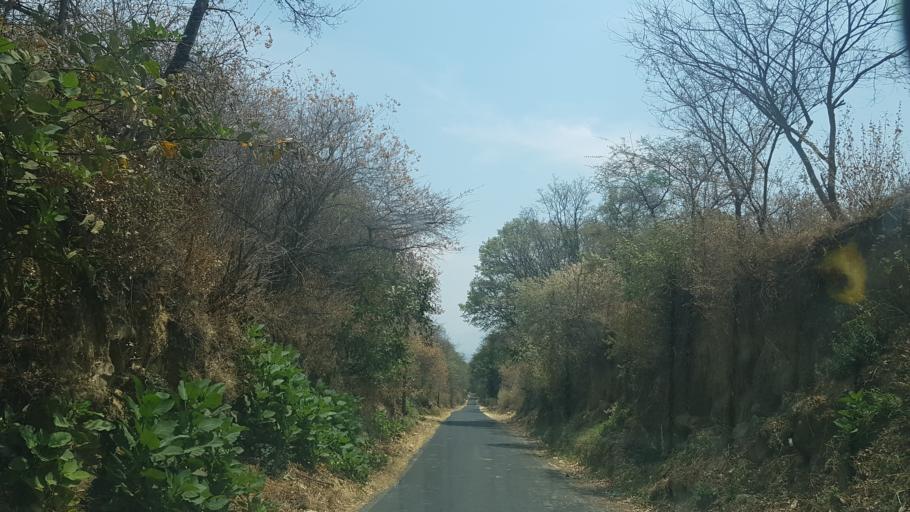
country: MX
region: Puebla
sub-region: Tochimilco
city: La Magdalena Yancuitlalpan
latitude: 18.8867
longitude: -98.5977
